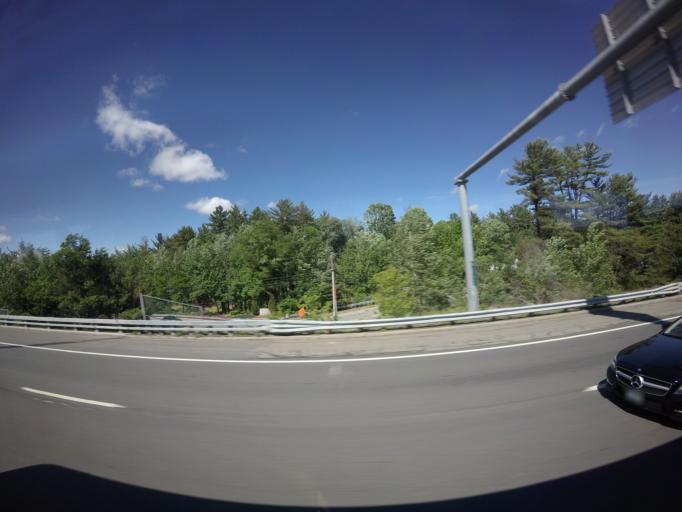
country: US
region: New Hampshire
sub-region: Hillsborough County
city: Manchester
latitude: 42.9541
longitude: -71.4029
